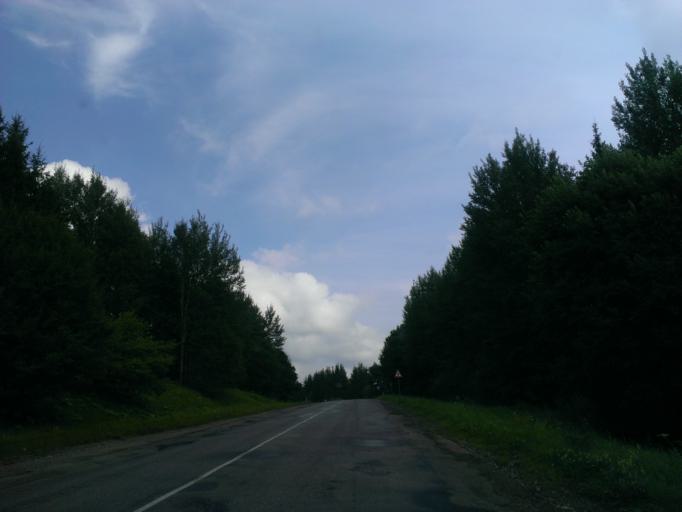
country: LV
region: Priekuli
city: Priekuli
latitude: 57.2688
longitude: 25.4617
